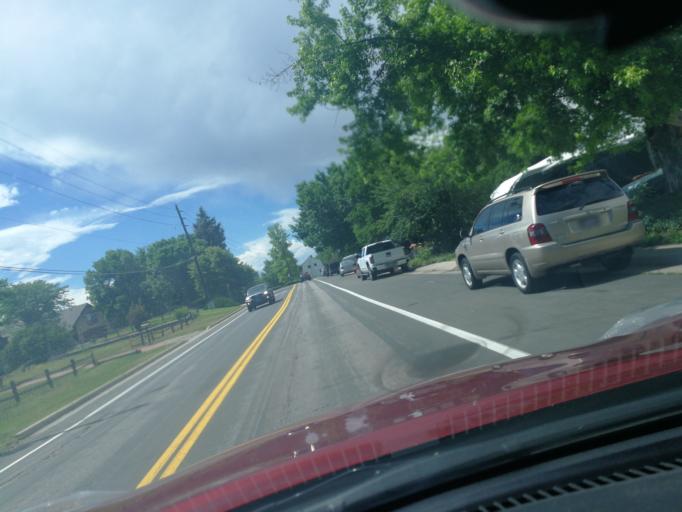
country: US
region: Colorado
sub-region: Arapahoe County
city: Littleton
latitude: 39.5930
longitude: -105.0013
